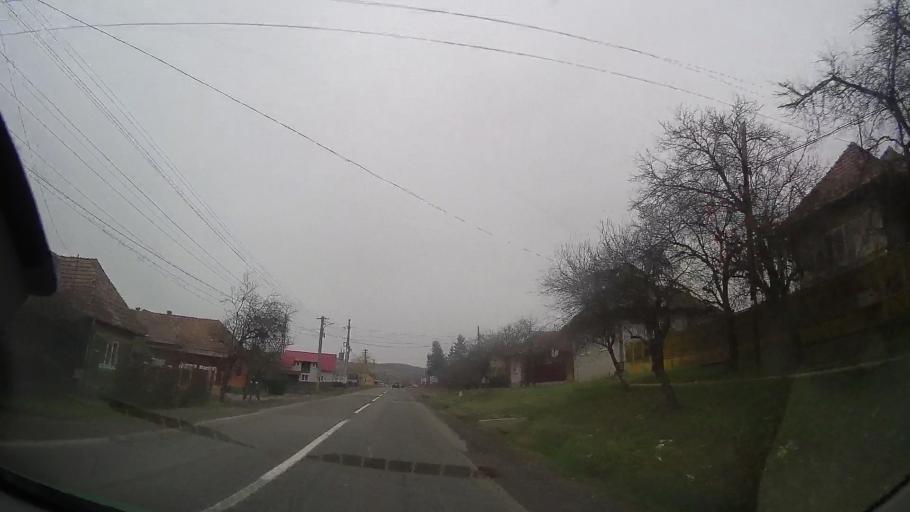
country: RO
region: Mures
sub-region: Comuna Ceausu de Campie
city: Ceausu de Campie
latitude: 46.6454
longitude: 24.4980
